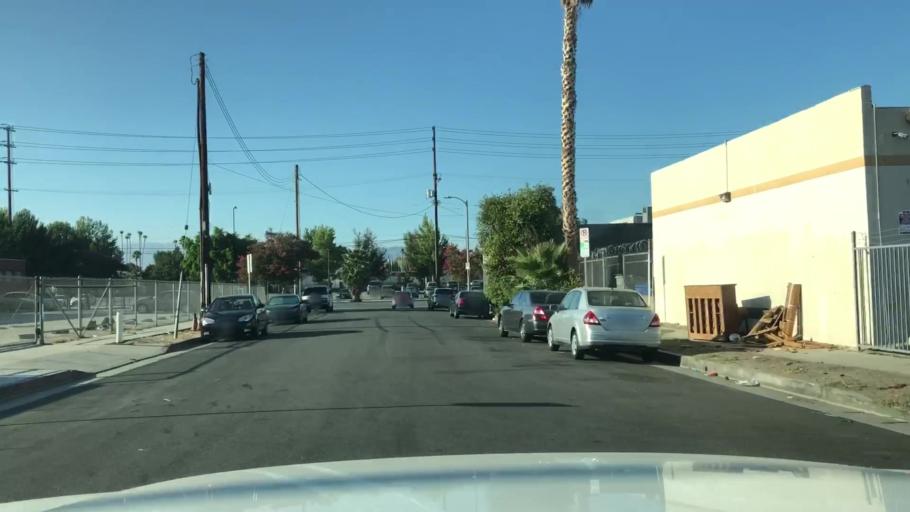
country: US
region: California
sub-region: Los Angeles County
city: Northridge
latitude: 34.1791
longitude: -118.5374
